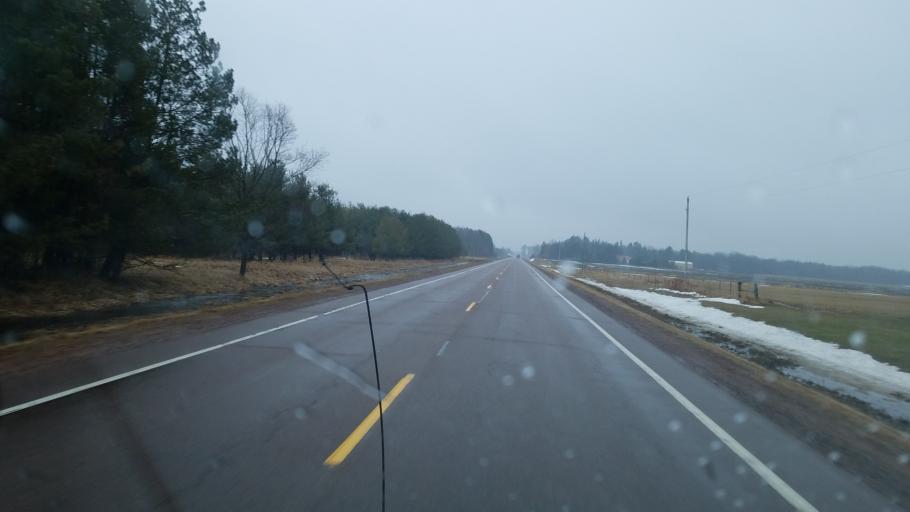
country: US
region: Wisconsin
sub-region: Wood County
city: Marshfield
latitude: 44.4535
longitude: -90.2881
